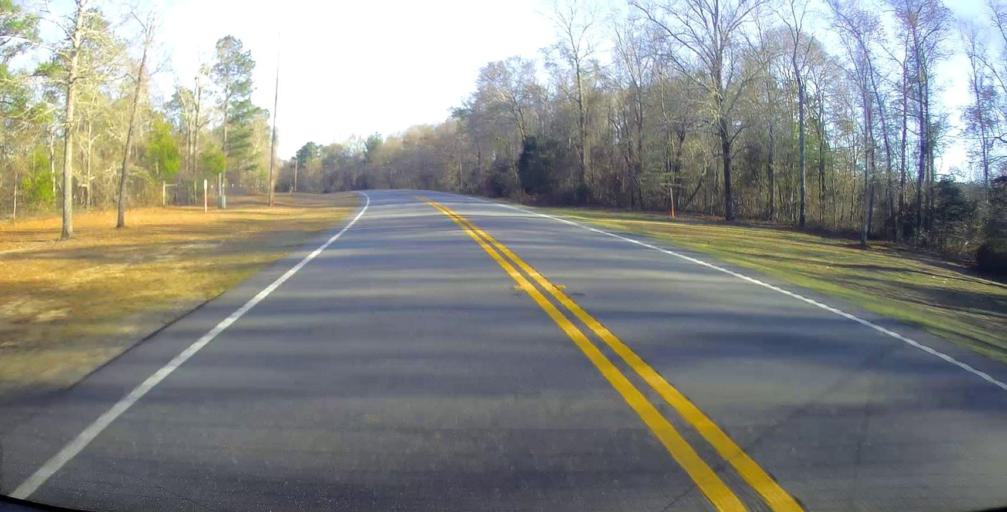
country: US
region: Georgia
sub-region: Taylor County
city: Butler
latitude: 32.4778
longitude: -84.3889
